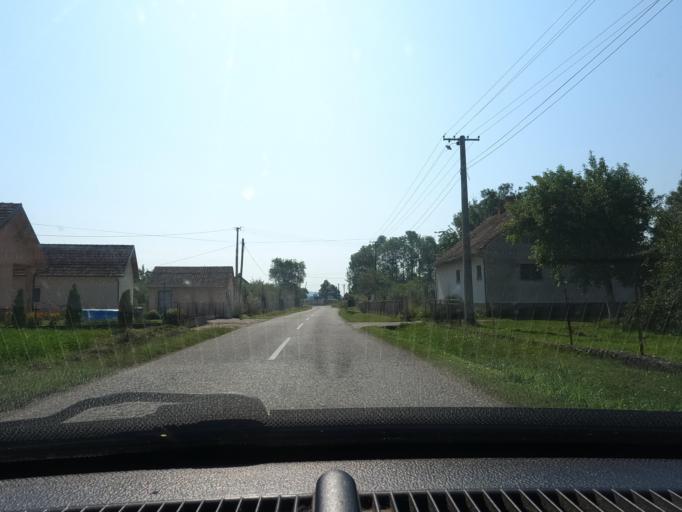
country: RS
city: Lipnicki Sor
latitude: 44.5779
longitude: 19.2711
